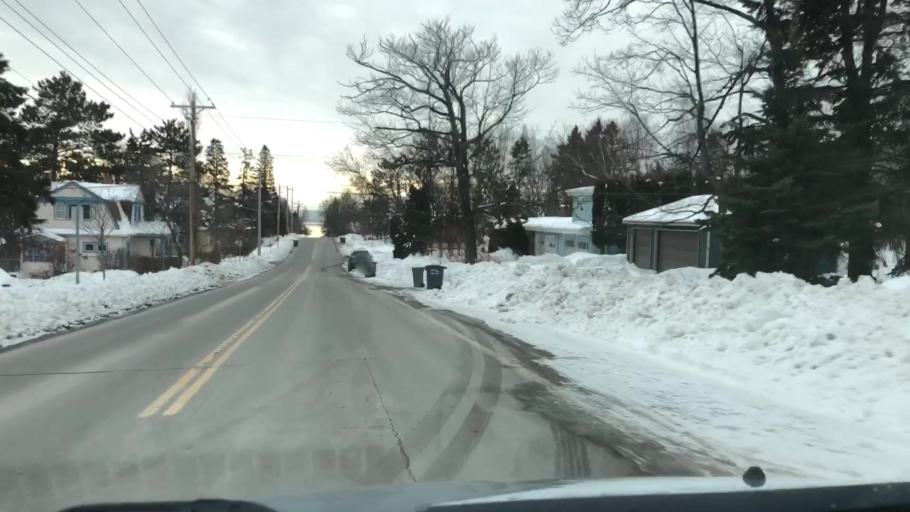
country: US
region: Minnesota
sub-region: Saint Louis County
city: Arnold
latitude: 46.8358
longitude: -92.0639
